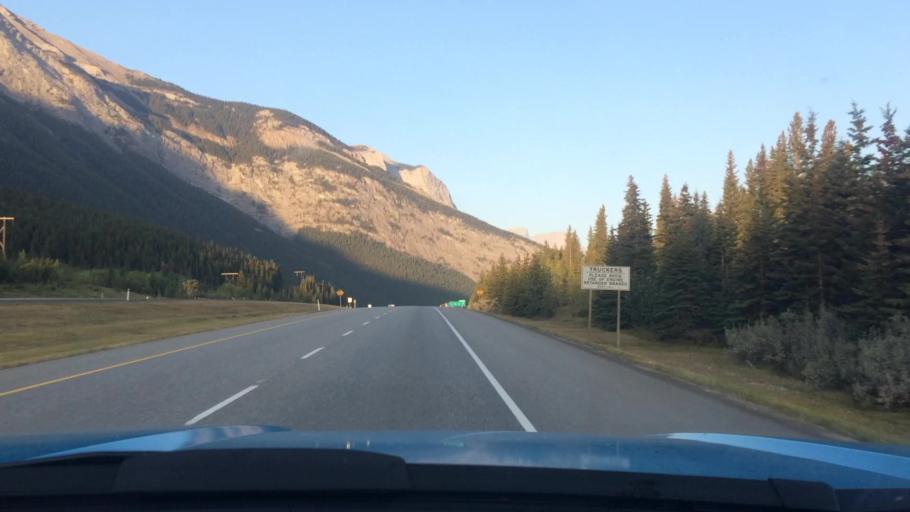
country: CA
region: Alberta
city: Canmore
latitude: 51.0525
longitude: -115.1526
